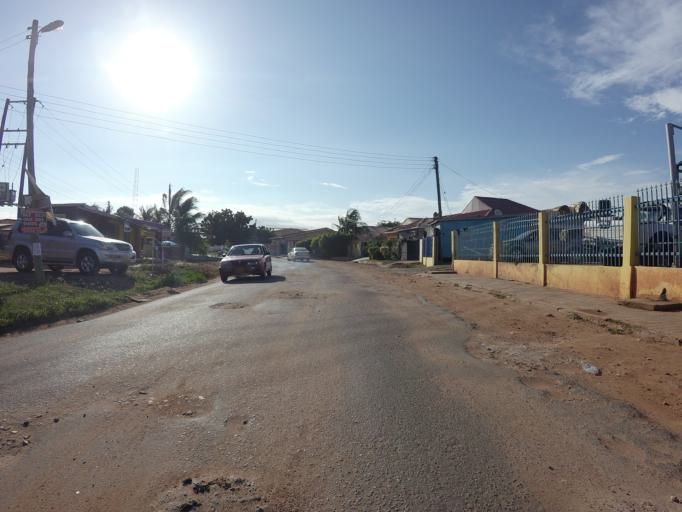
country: GH
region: Greater Accra
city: Tema
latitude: 5.6527
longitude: -0.0649
